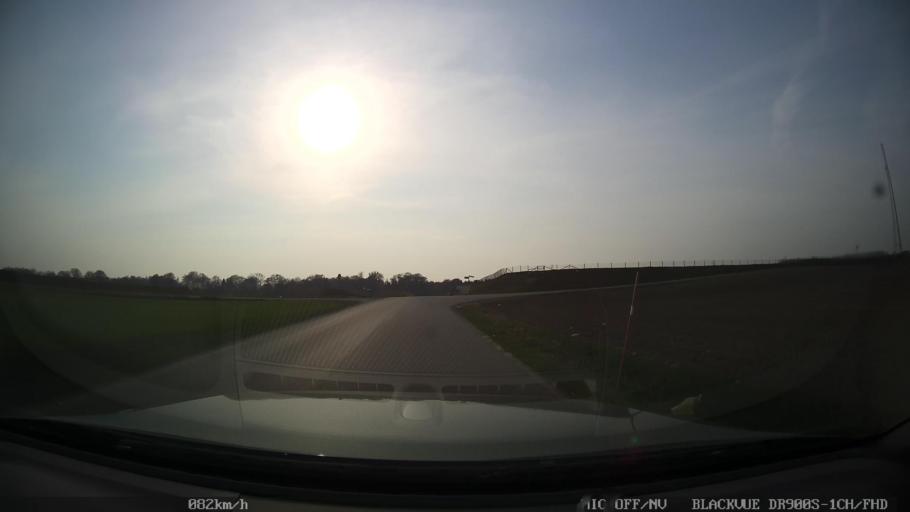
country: SE
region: Skane
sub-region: Ystads Kommun
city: Ystad
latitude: 55.4594
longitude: 13.7881
